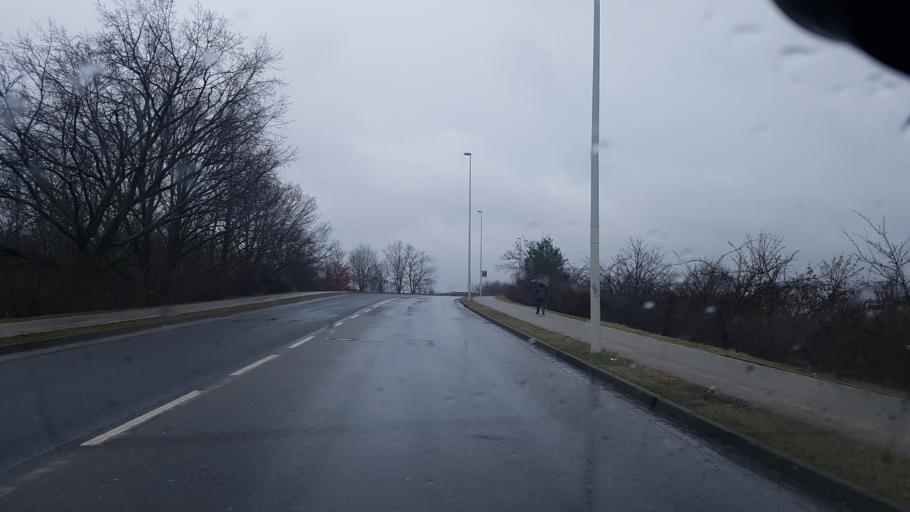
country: DE
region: Brandenburg
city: Cottbus
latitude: 51.7214
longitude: 14.3189
